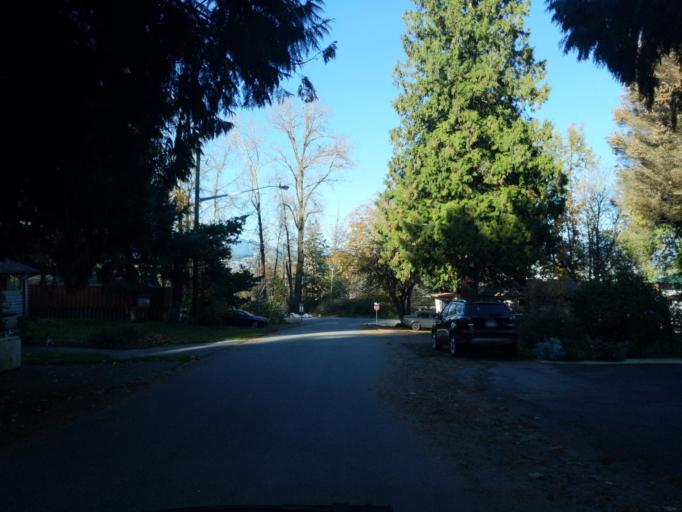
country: CA
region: British Columbia
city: New Westminster
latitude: 49.2056
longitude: -122.8577
